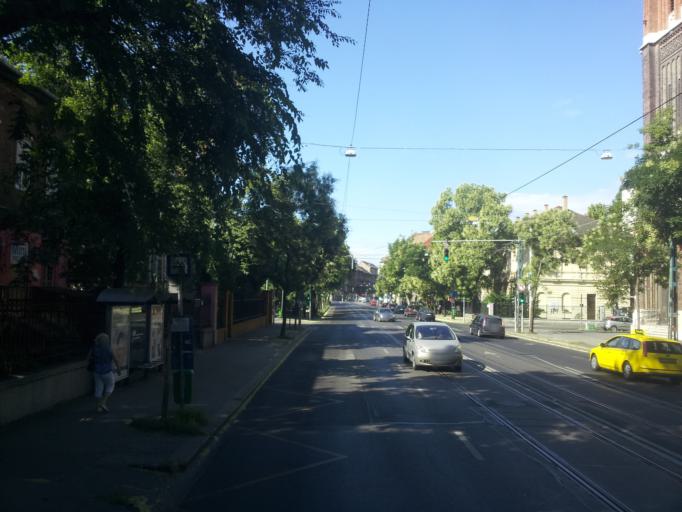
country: HU
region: Budapest
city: Budapest XIV. keruelet
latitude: 47.5057
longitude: 19.0916
